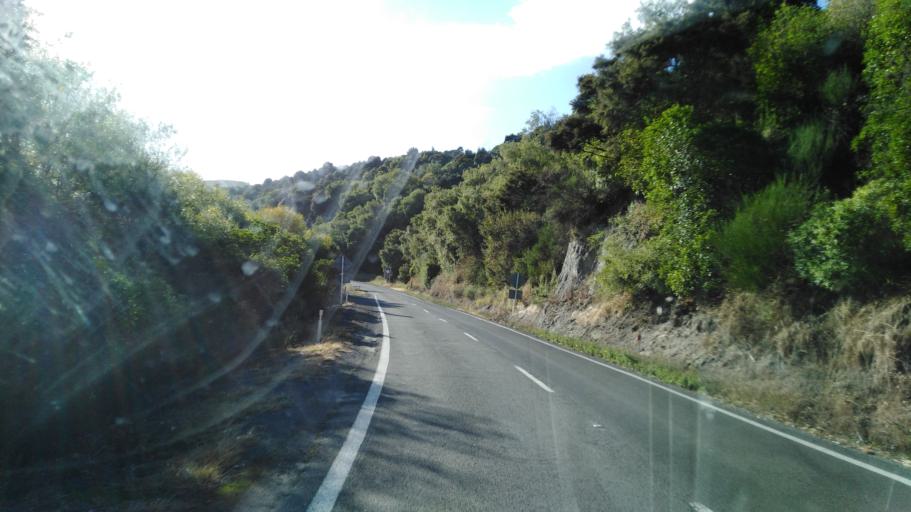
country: NZ
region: Waikato
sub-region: Taupo District
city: Taupo
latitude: -38.8765
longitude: 175.9926
